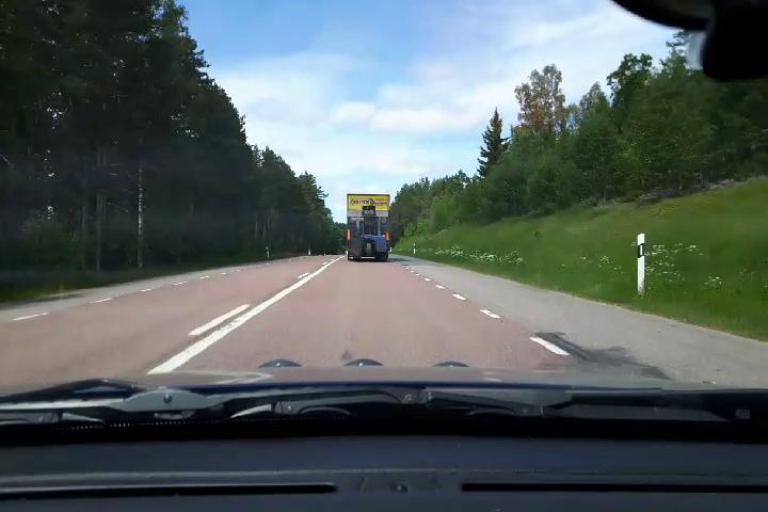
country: SE
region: Uppsala
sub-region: Osthammars Kommun
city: Bjorklinge
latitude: 60.1383
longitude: 17.5057
